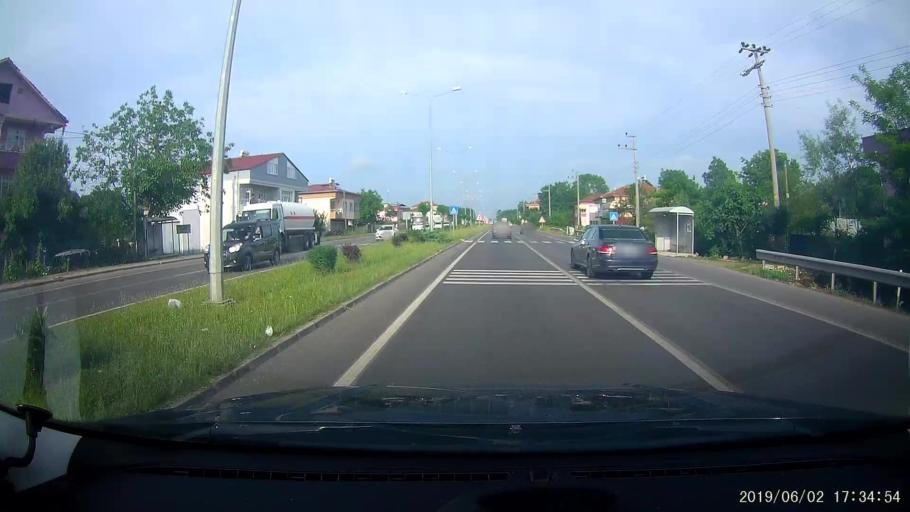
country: TR
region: Samsun
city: Terme
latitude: 41.2198
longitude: 36.8775
